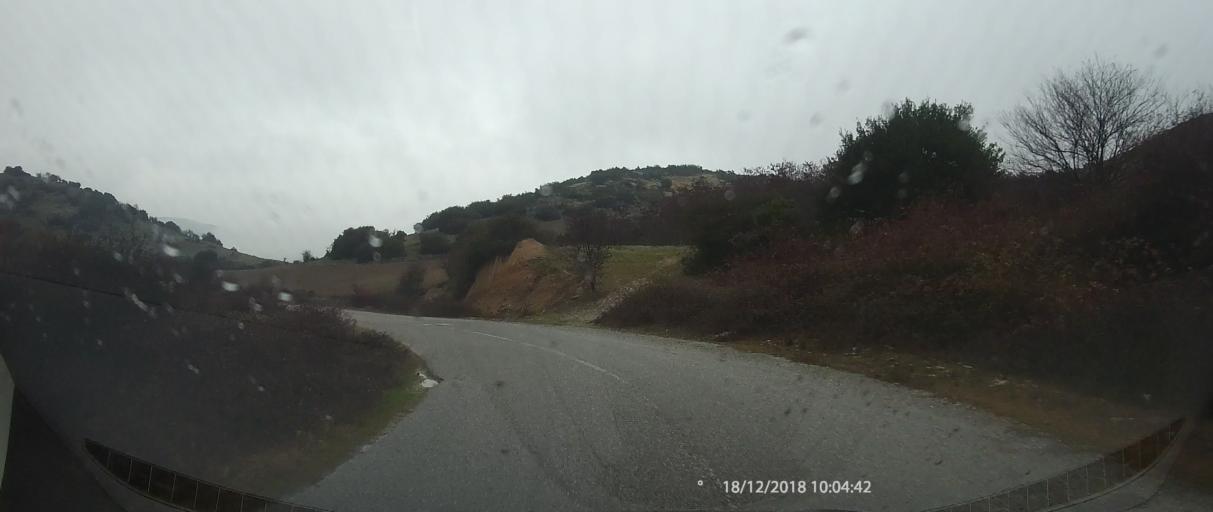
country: GR
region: Thessaly
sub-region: Nomos Larisis
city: Livadi
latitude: 40.0550
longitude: 22.2223
